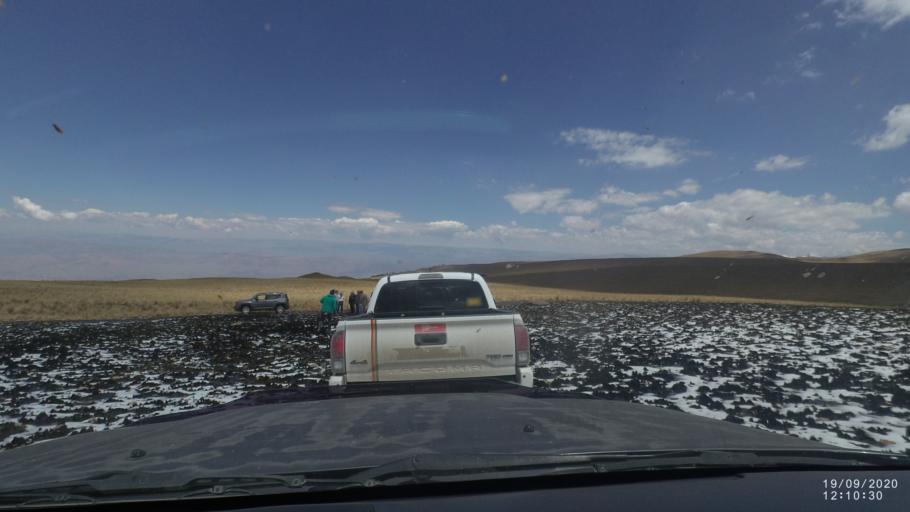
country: BO
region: Cochabamba
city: Cochabamba
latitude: -17.3001
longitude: -66.1076
